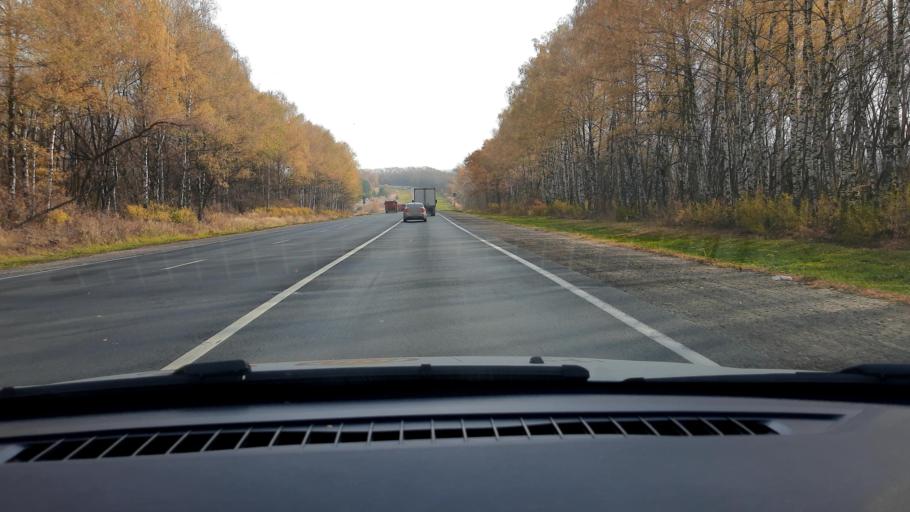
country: RU
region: Nizjnij Novgorod
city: Pamyat' Parizhskoy Kommuny
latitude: 56.0508
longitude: 44.4123
